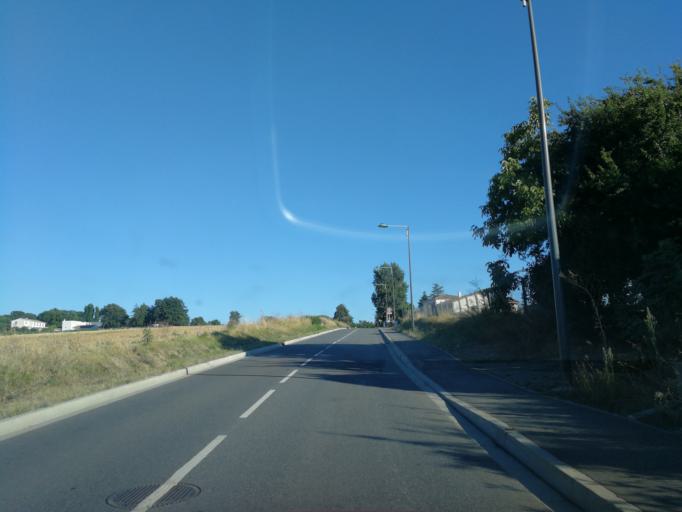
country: FR
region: Midi-Pyrenees
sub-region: Departement de la Haute-Garonne
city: Balma
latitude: 43.6238
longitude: 1.4982
